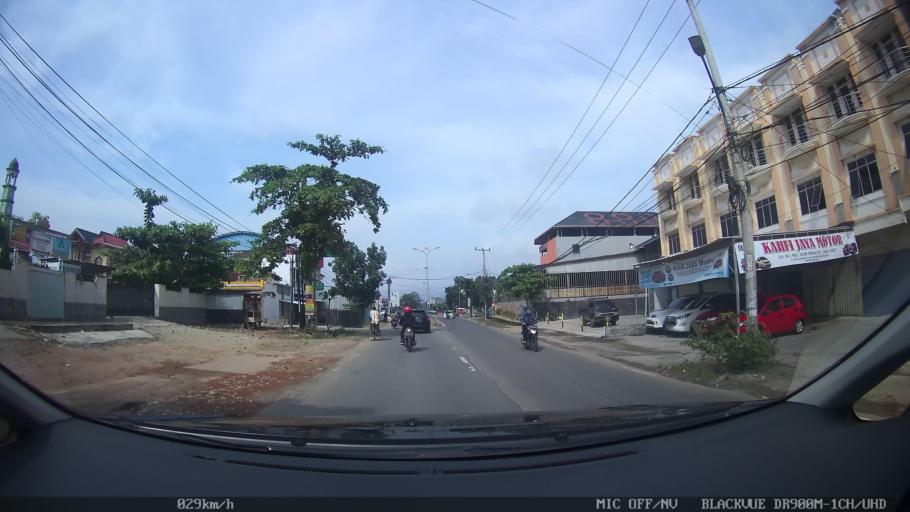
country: ID
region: Lampung
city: Kedaton
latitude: -5.3888
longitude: 105.2893
